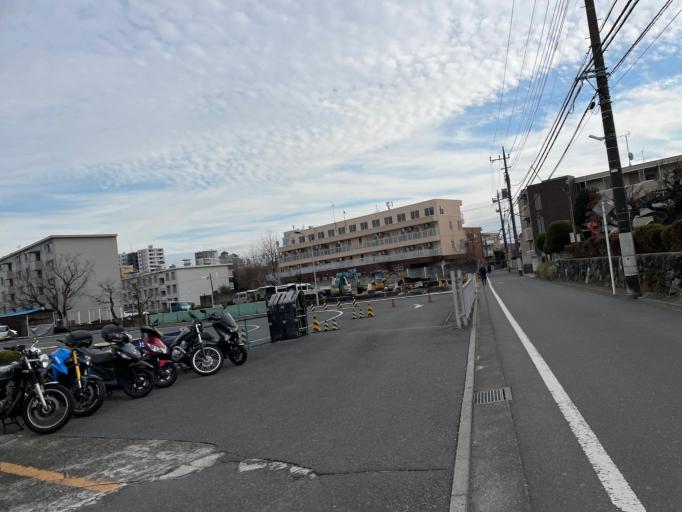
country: JP
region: Tokyo
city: Kamirenjaku
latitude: 35.7054
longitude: 139.5395
